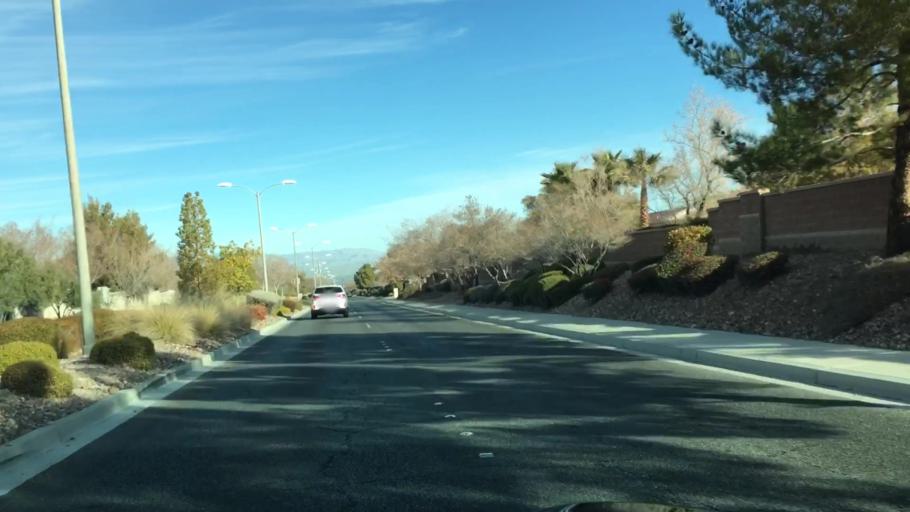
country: US
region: Nevada
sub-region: Clark County
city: Whitney
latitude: 35.9718
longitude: -115.1008
